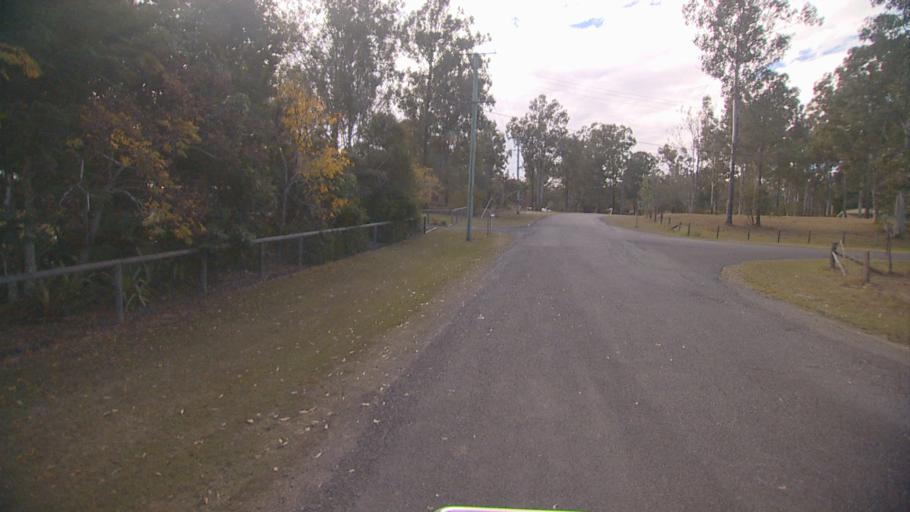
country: AU
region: Queensland
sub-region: Logan
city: North Maclean
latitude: -27.8199
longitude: 153.0456
